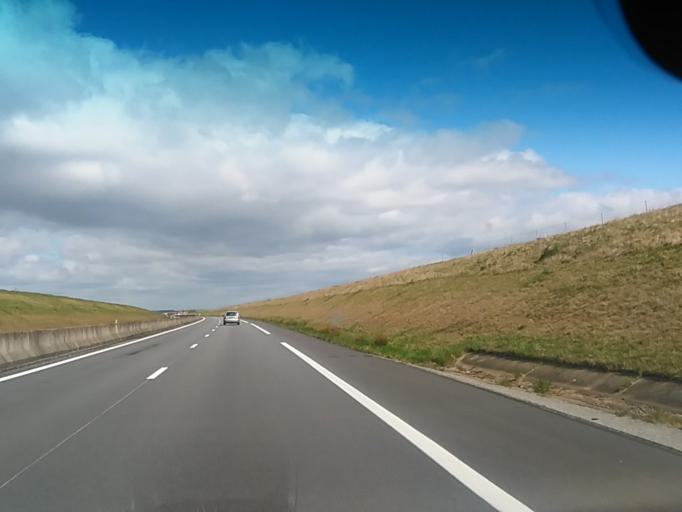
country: FR
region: Lower Normandy
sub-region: Departement du Calvados
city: Orbec
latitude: 49.0596
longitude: 0.4653
